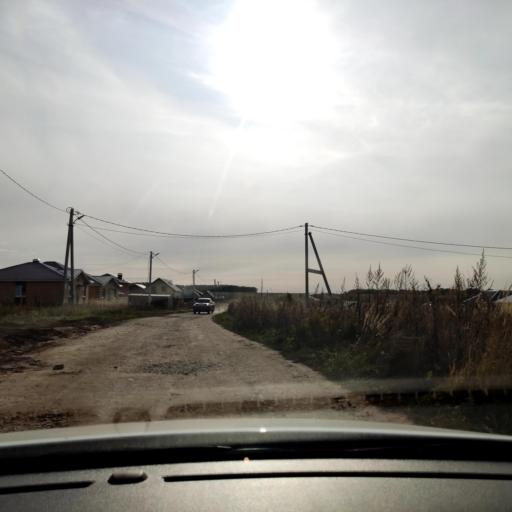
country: RU
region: Tatarstan
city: Vysokaya Gora
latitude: 55.8661
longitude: 49.3688
